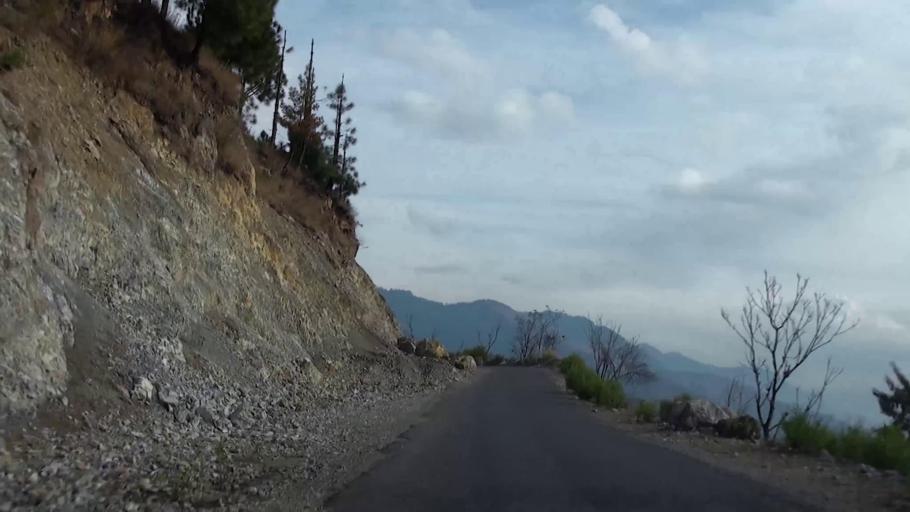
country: PK
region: Azad Kashmir
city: Muzaffarabad
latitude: 34.3660
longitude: 73.5004
